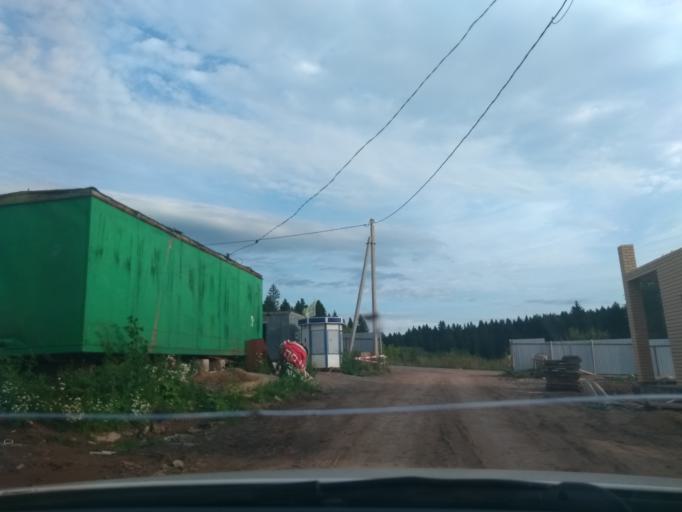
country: RU
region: Perm
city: Perm
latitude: 57.9985
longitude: 56.3221
